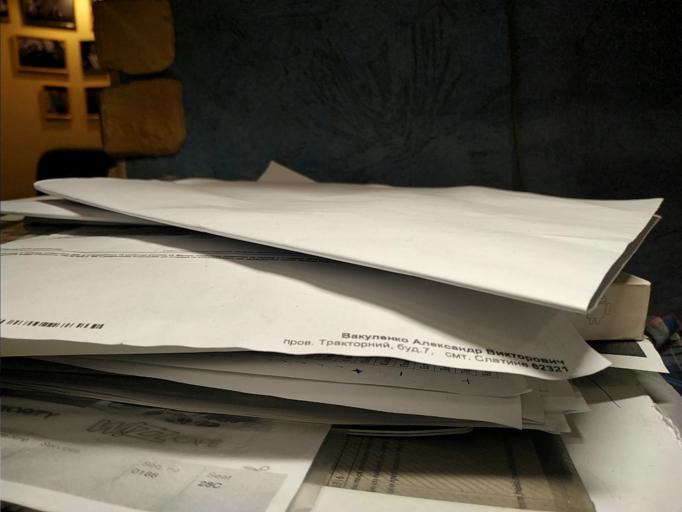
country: RU
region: Tverskaya
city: Zubtsov
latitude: 56.0889
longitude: 34.7526
